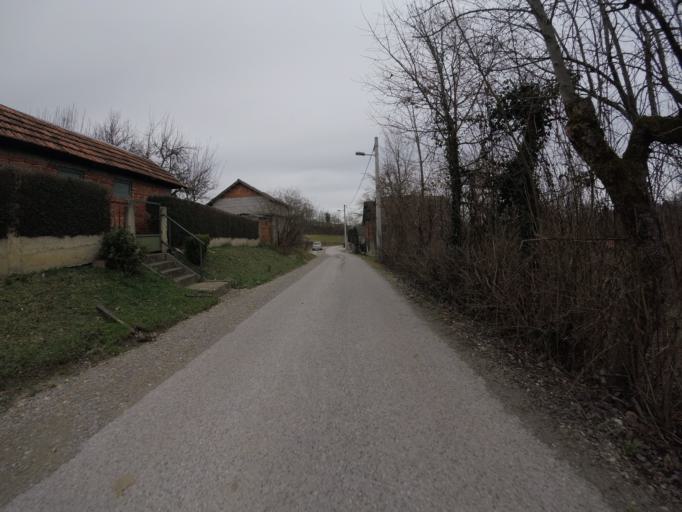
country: HR
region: Grad Zagreb
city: Strmec
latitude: 45.6640
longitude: 15.8749
